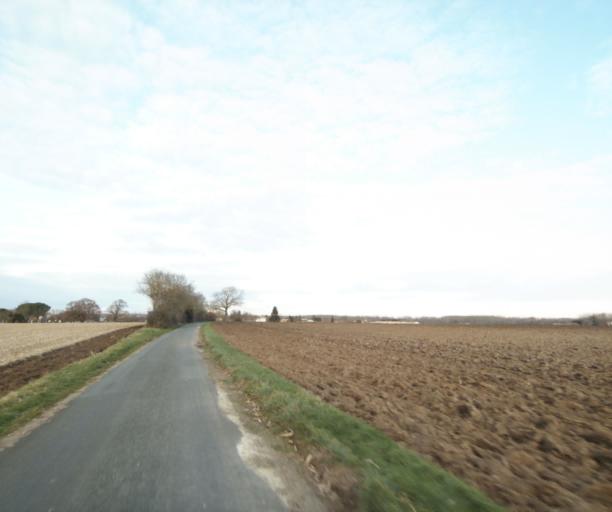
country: FR
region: Poitou-Charentes
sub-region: Departement de la Charente-Maritime
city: Les Gonds
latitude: 45.7075
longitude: -0.6130
